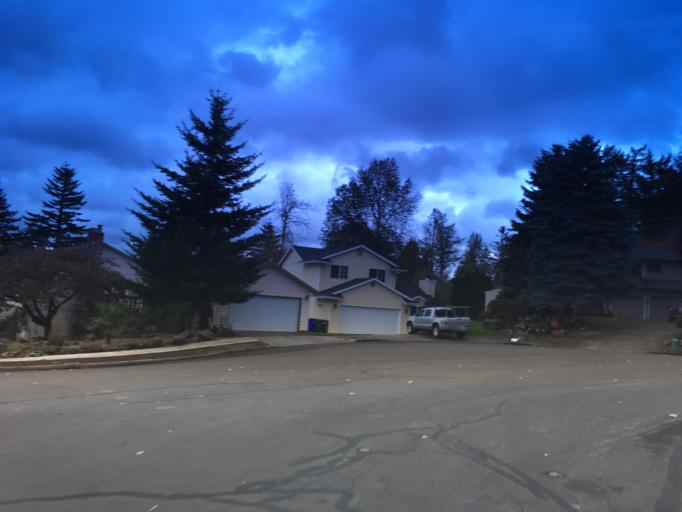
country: US
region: Oregon
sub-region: Multnomah County
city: Fairview
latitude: 45.5359
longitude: -122.4439
